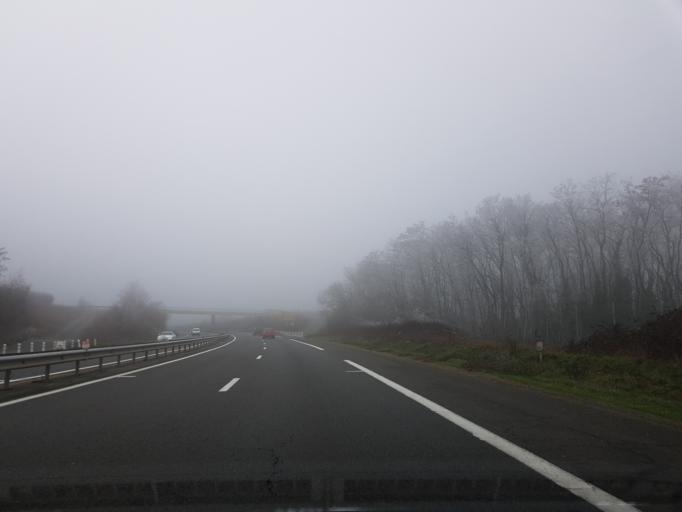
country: FR
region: Bourgogne
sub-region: Departement de Saone-et-Loire
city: Ecuisses
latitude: 46.7435
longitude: 4.5476
